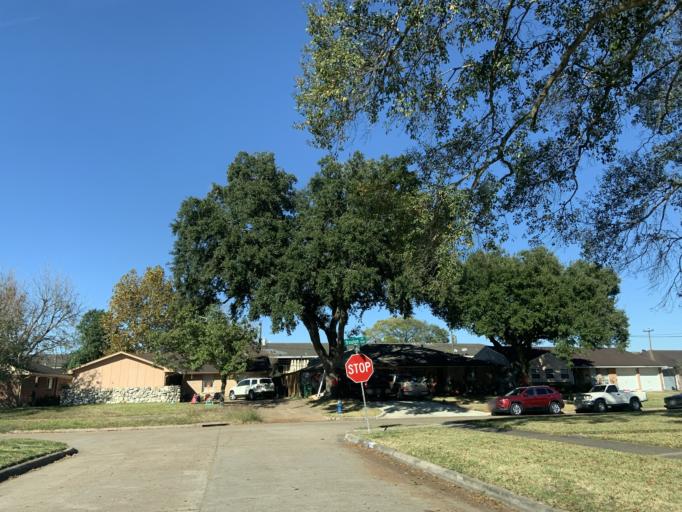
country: US
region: Texas
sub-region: Harris County
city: Bellaire
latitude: 29.6900
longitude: -95.5128
